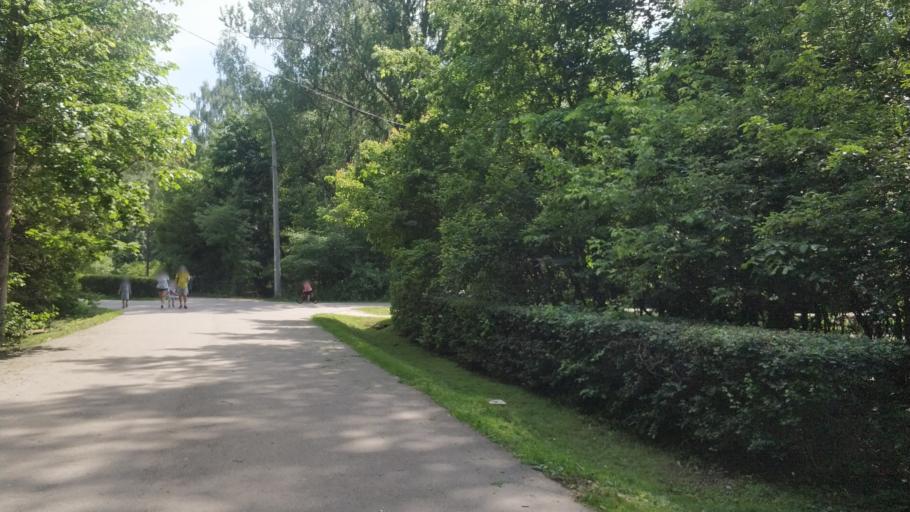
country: RU
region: Moscow
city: Perovo
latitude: 55.7343
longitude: 37.7983
